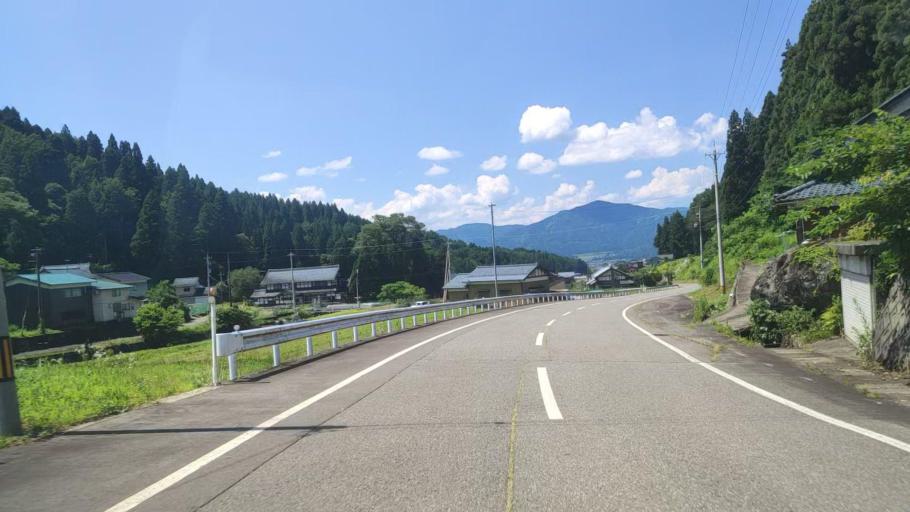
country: JP
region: Fukui
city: Katsuyama
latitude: 36.1070
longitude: 136.4972
